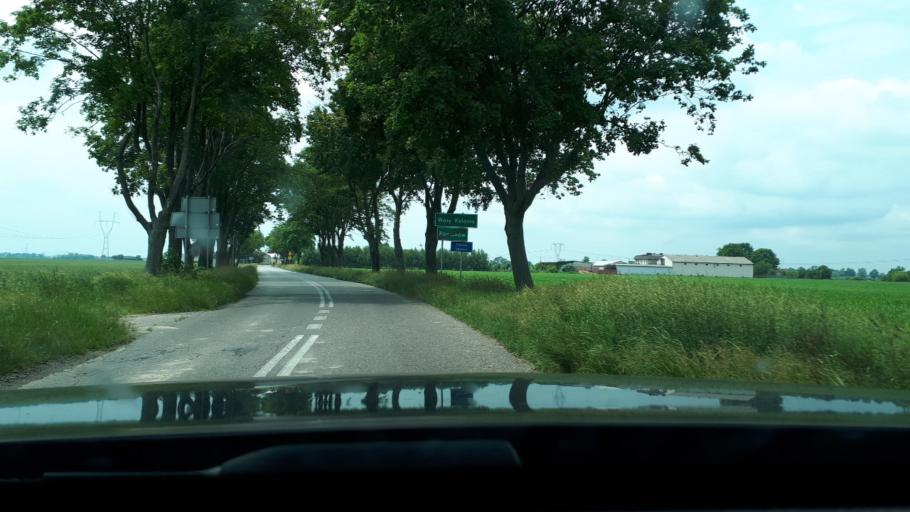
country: PL
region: Masovian Voivodeship
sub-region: Powiat warszawski zachodni
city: Jozefow
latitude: 52.2365
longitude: 20.6625
